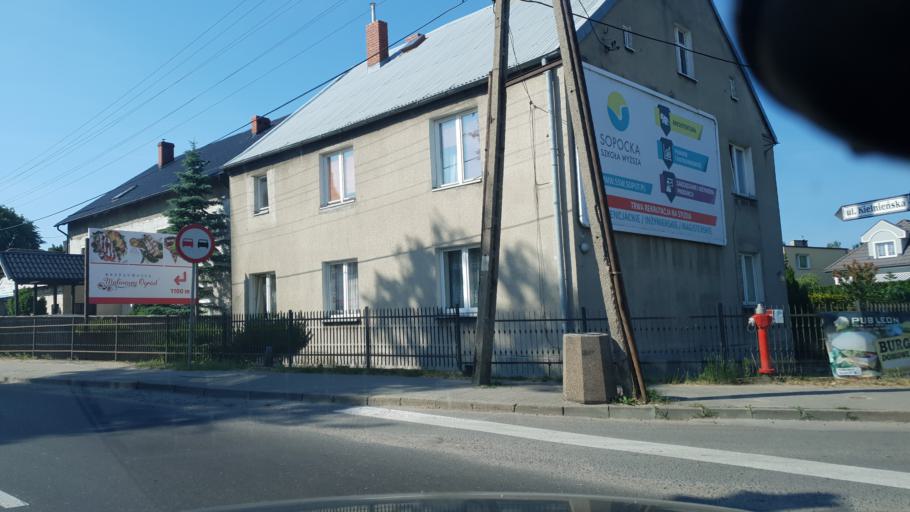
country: PL
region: Pomeranian Voivodeship
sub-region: Gdynia
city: Wielki Kack
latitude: 54.4346
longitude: 18.4667
